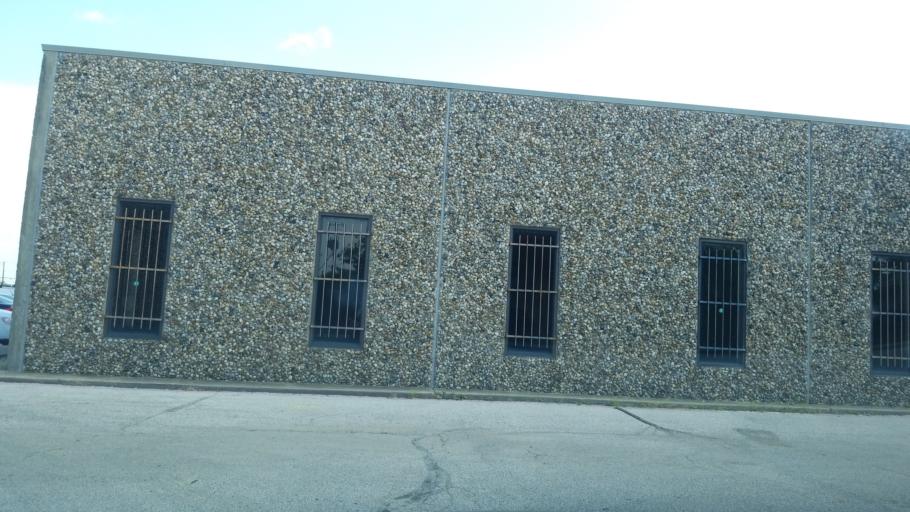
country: US
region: Texas
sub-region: Dallas County
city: Farmers Branch
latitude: 32.8797
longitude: -96.8885
